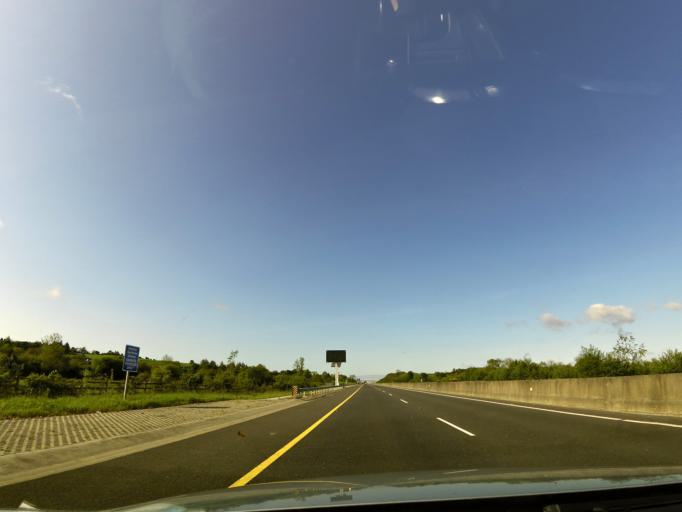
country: IE
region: Munster
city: Ballina
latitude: 52.7777
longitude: -8.3772
